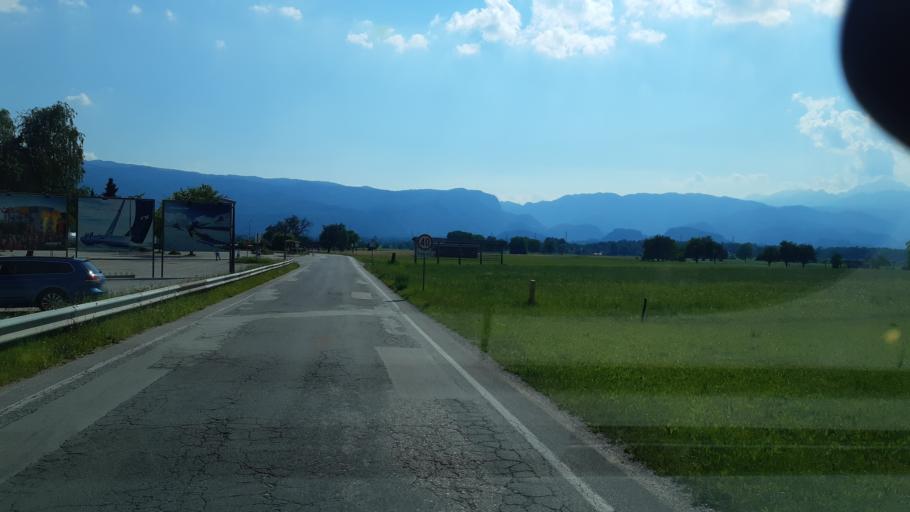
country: SI
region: Radovljica
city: Radovljica
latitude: 46.3722
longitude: 14.1955
